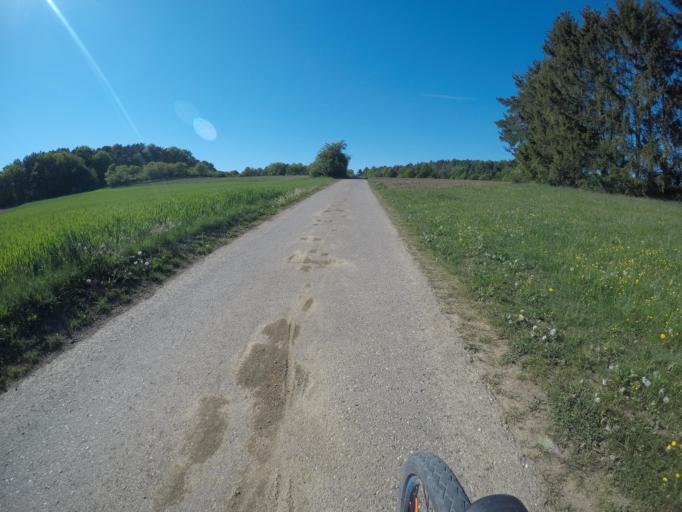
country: DE
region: Baden-Wuerttemberg
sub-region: Karlsruhe Region
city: Friolzheim
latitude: 48.8223
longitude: 8.8516
